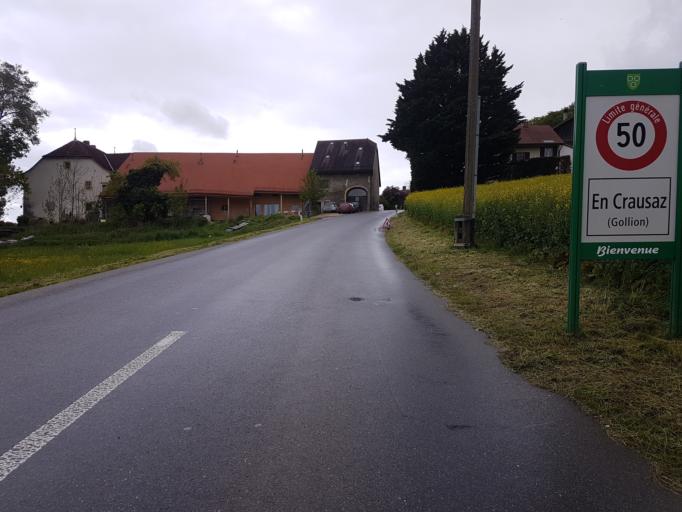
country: CH
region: Vaud
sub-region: Gros-de-Vaud District
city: Penthalaz
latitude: 46.5957
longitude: 6.5269
